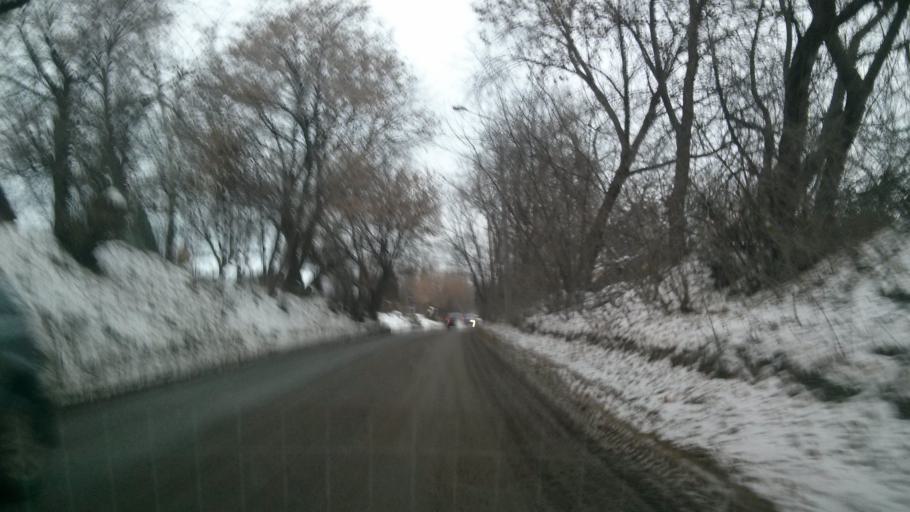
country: RU
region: Nizjnij Novgorod
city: Afonino
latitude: 56.2941
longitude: 44.0942
